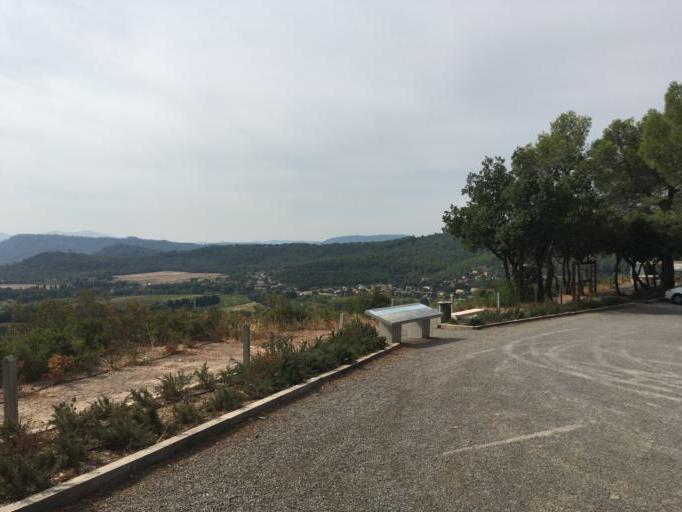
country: FR
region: Provence-Alpes-Cote d'Azur
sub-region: Departement du Var
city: Taradeau
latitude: 43.4533
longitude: 6.4347
